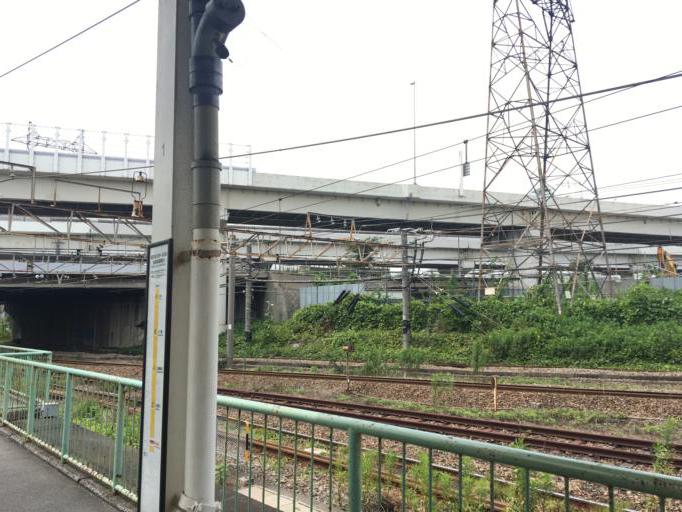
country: JP
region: Kanagawa
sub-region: Kawasaki-shi
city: Kawasaki
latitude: 35.5104
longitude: 139.7134
